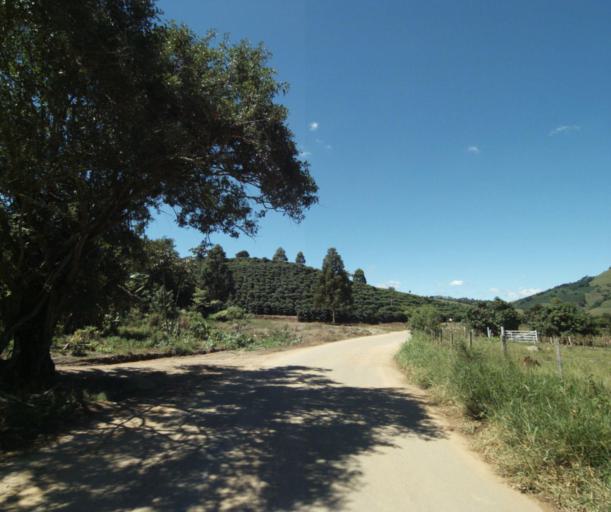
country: BR
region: Minas Gerais
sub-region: Espera Feliz
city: Espera Feliz
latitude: -20.6151
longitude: -41.8381
